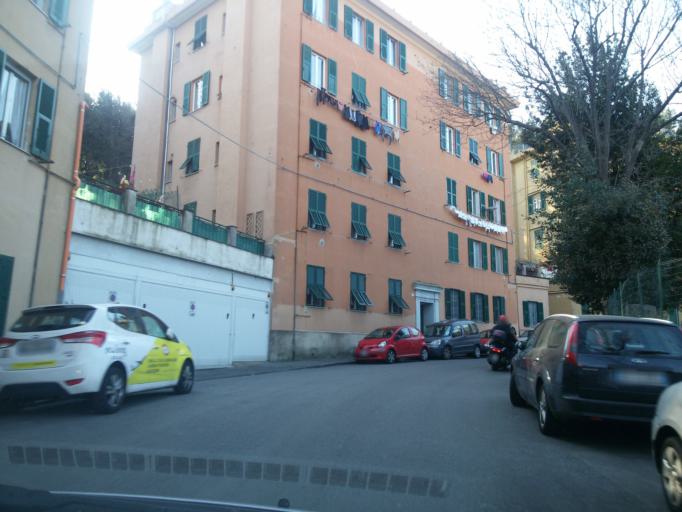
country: IT
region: Liguria
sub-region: Provincia di Genova
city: Genoa
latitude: 44.4169
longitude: 8.9442
